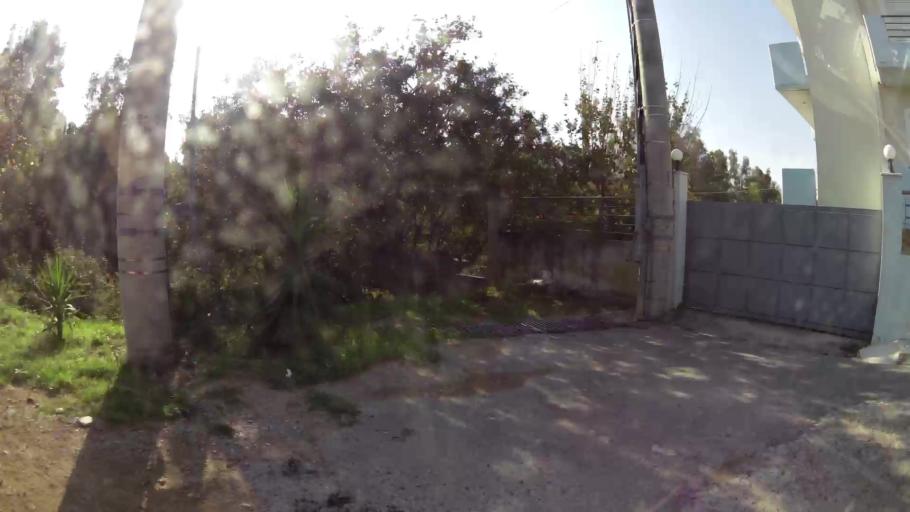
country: GR
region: Attica
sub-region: Nomarchia Athinas
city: Nea Filadelfeia
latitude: 38.0529
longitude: 23.7397
